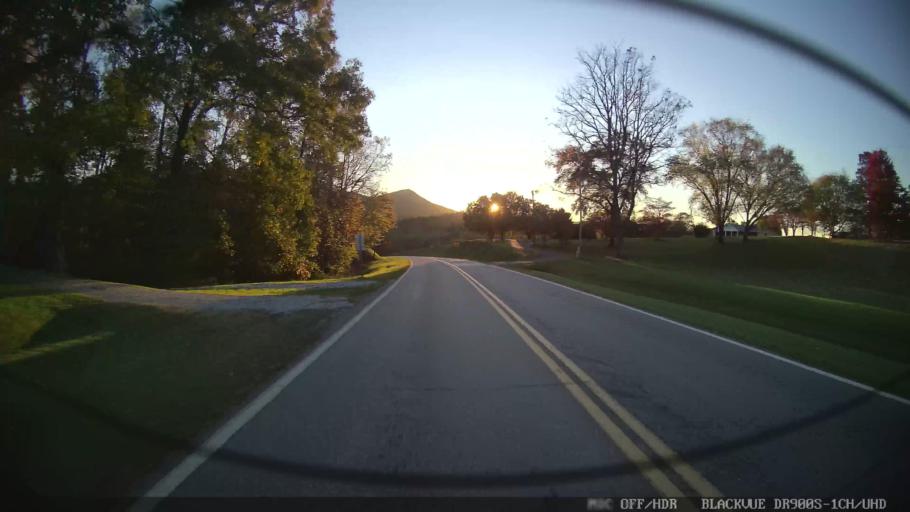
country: US
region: Georgia
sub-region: Union County
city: Blairsville
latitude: 34.8450
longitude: -83.9325
